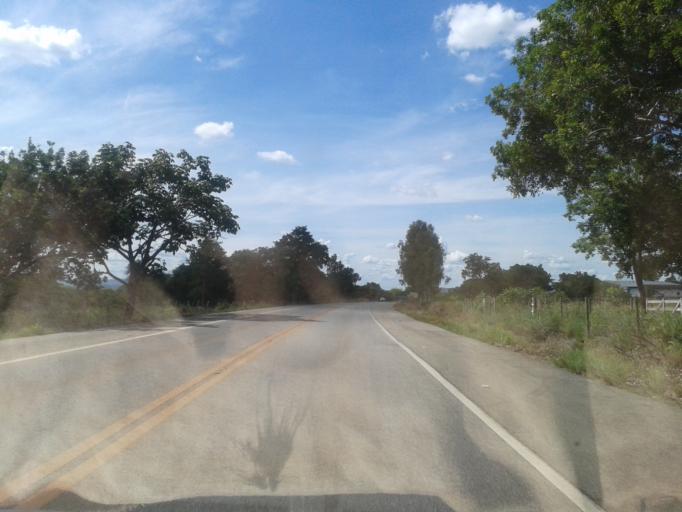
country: BR
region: Goias
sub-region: Itapuranga
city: Itapuranga
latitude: -15.4655
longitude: -50.3519
